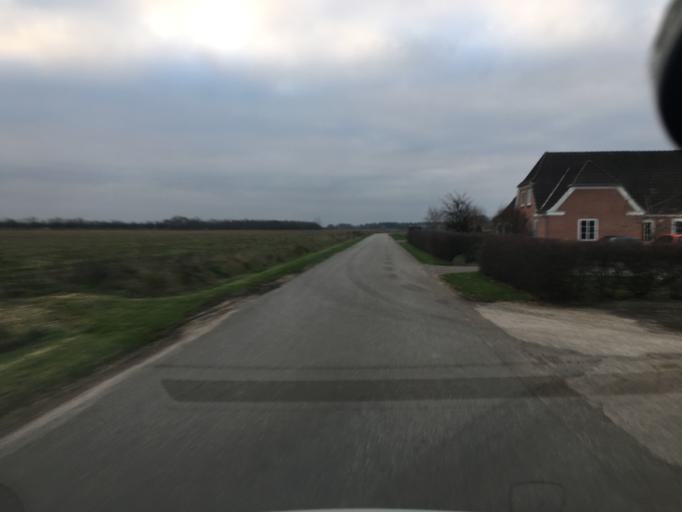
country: DK
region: South Denmark
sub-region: Tonder Kommune
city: Logumkloster
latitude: 55.0652
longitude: 9.0662
